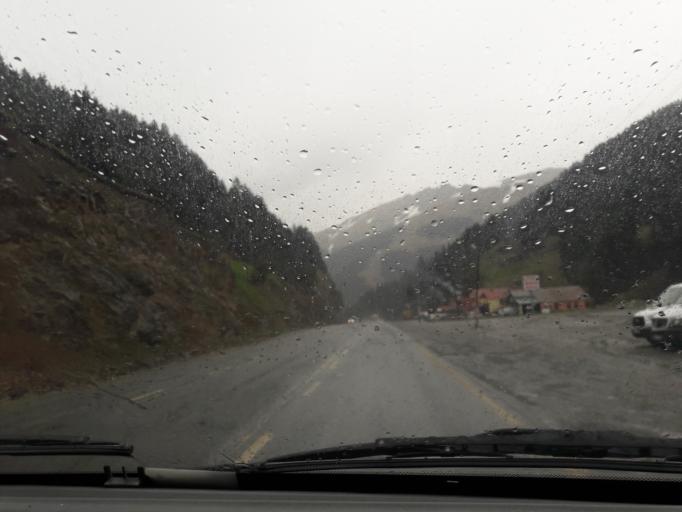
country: TR
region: Gumushane
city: Yaglidere
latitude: 40.6745
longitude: 39.4241
